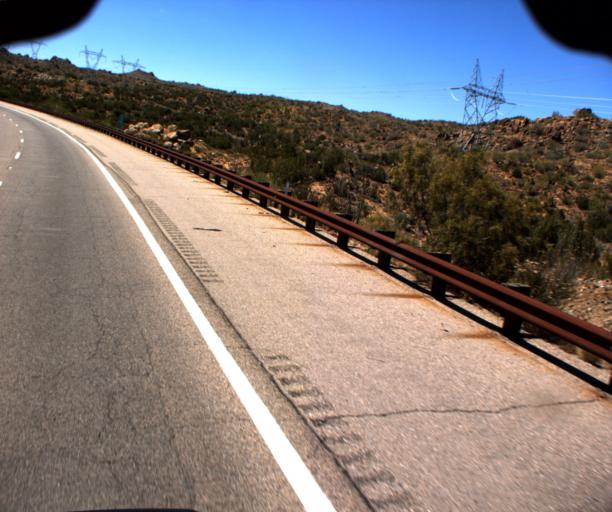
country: US
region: Arizona
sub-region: Yavapai County
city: Bagdad
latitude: 34.4620
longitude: -113.2958
